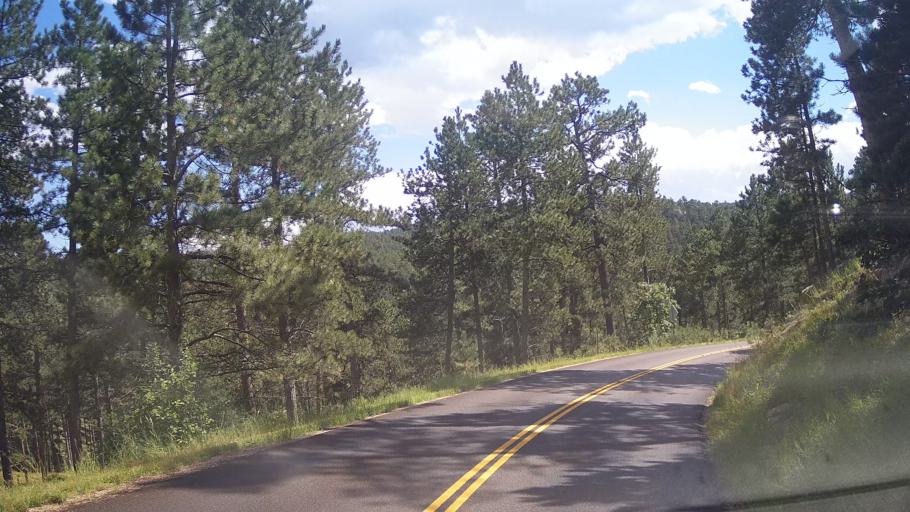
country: US
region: South Dakota
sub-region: Pennington County
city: Colonial Pine Hills
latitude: 43.8821
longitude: -103.4367
